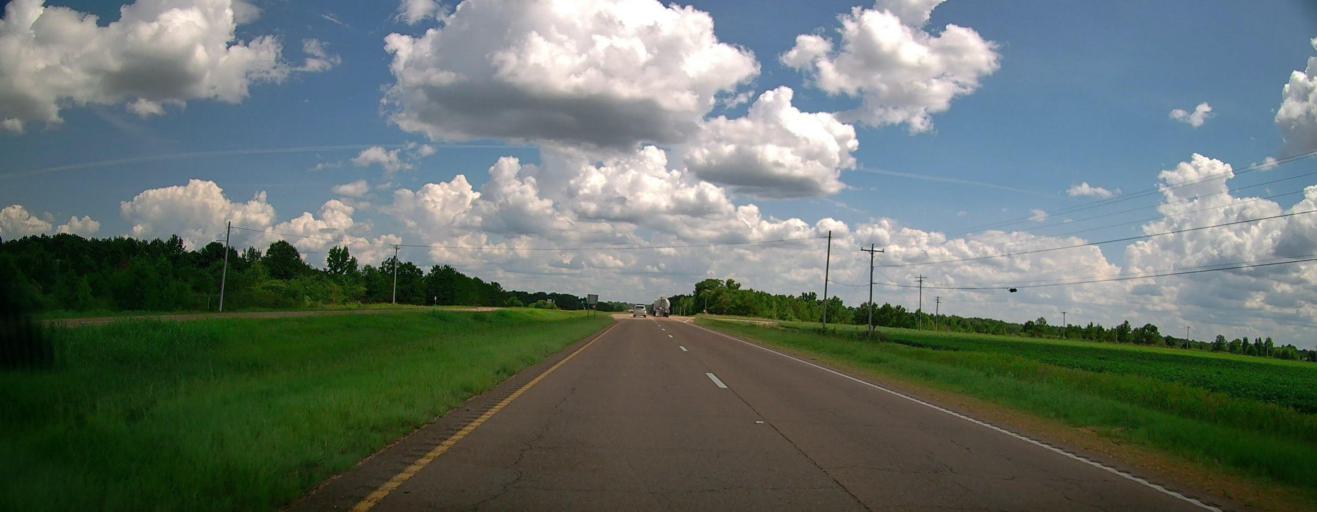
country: US
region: Mississippi
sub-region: Lowndes County
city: Columbus Air Force Base
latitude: 33.6903
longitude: -88.4387
